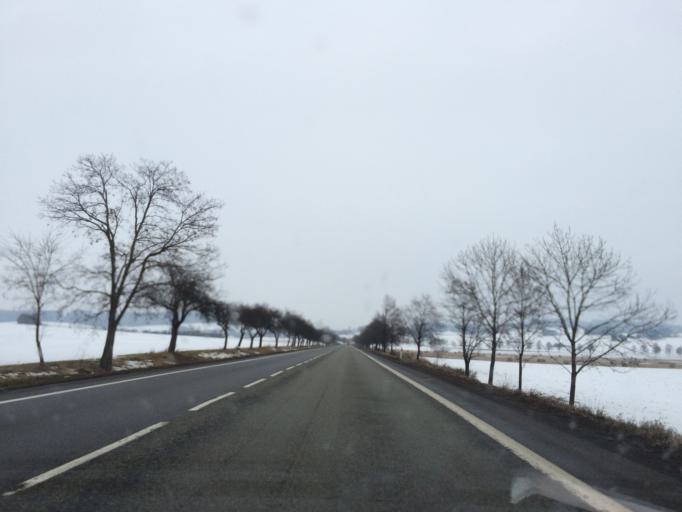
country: CZ
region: Jihocesky
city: Radomysl
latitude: 49.2863
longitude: 13.9631
